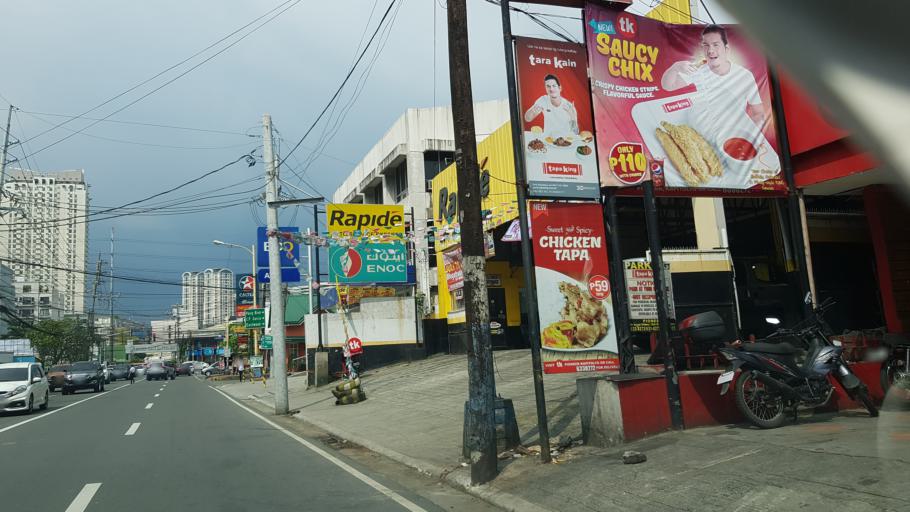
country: PH
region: Metro Manila
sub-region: Pasig
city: Pasig City
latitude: 14.5754
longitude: 121.0586
